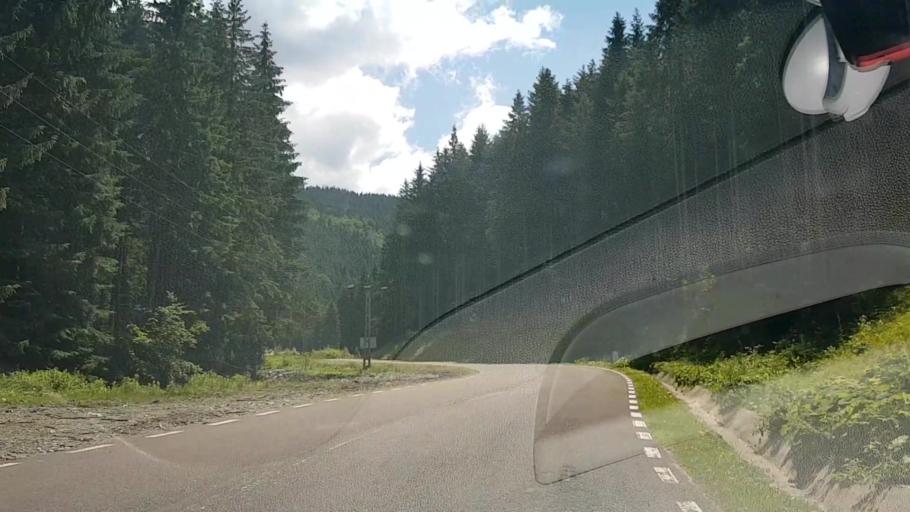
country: RO
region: Suceava
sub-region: Comuna Sadova
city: Sadova
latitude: 47.4727
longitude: 25.5050
